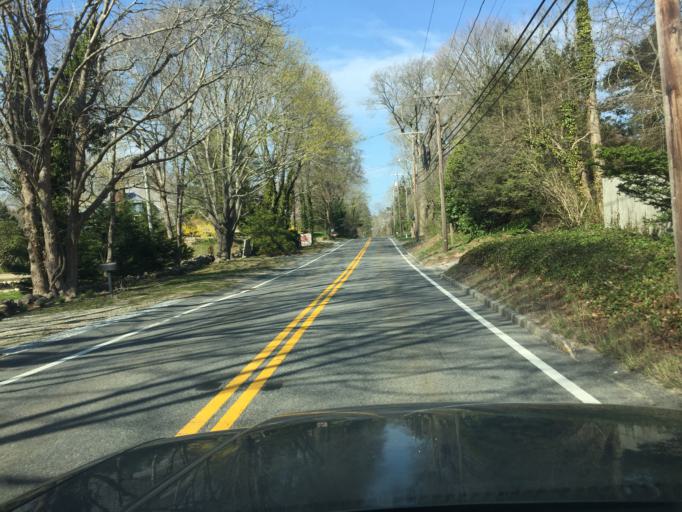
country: US
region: Massachusetts
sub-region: Barnstable County
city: Falmouth
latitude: 41.5361
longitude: -70.6516
